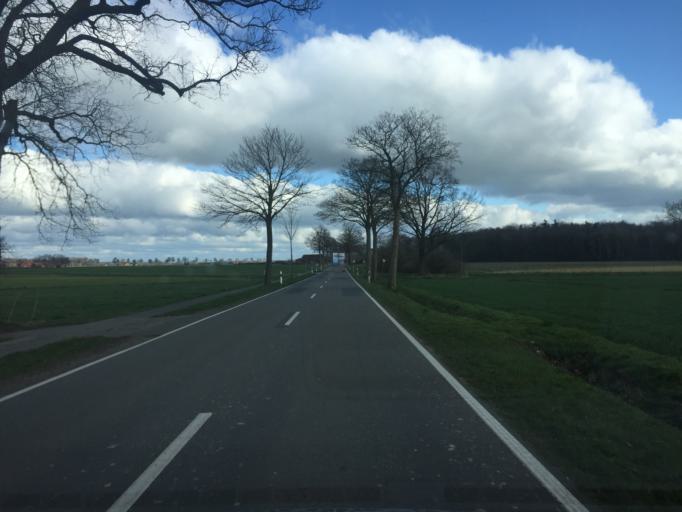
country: DE
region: Lower Saxony
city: Schwaforden
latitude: 52.7651
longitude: 8.8490
